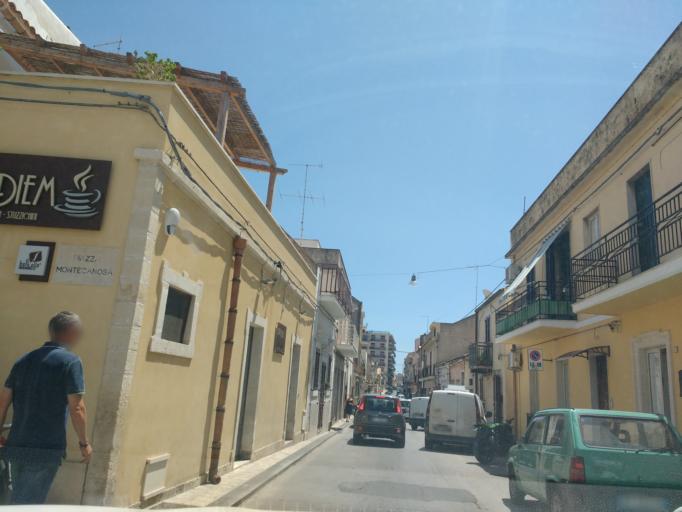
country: IT
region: Sicily
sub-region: Provincia di Siracusa
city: Noto
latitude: 36.8901
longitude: 15.0648
